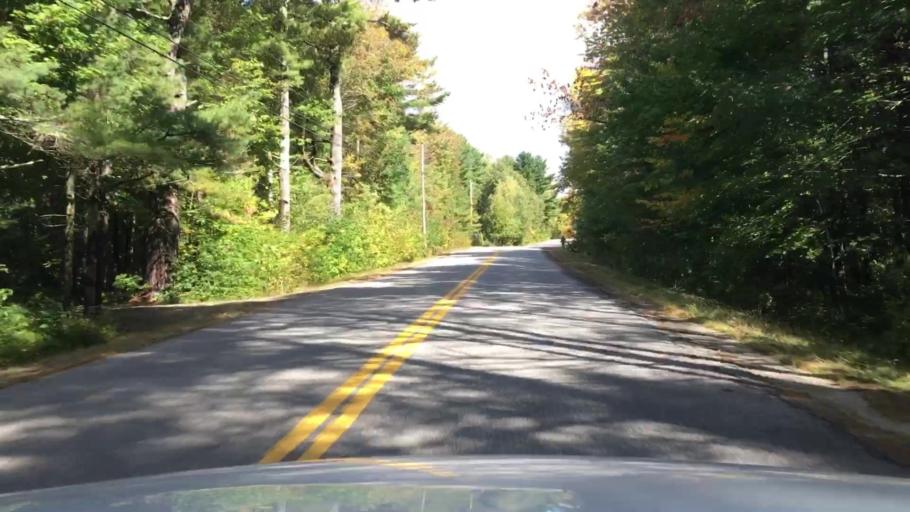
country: US
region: Maine
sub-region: Cumberland County
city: Brunswick
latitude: 43.9464
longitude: -69.8964
